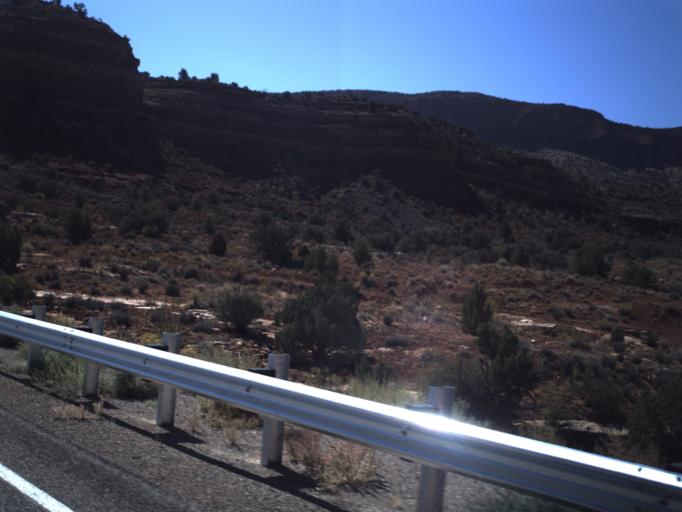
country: US
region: Utah
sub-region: San Juan County
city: Blanding
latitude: 37.7428
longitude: -110.2804
